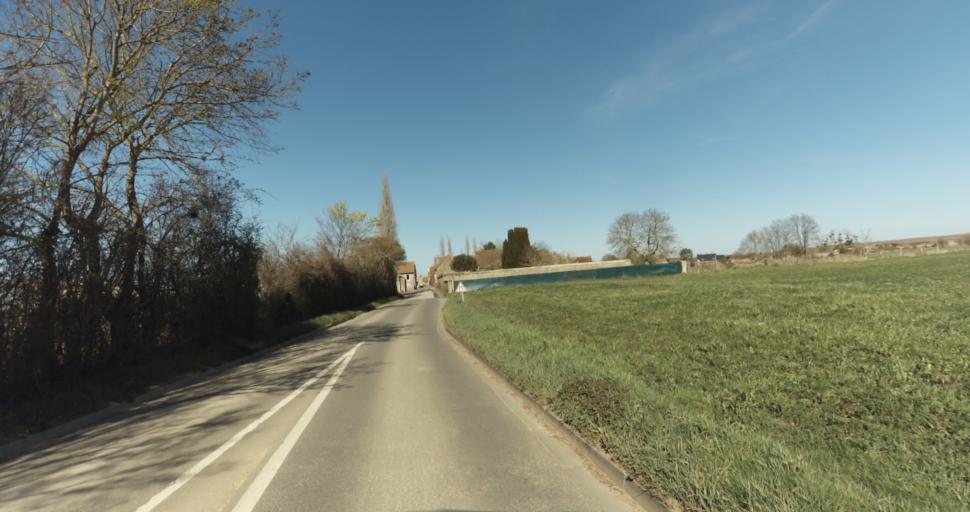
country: FR
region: Lower Normandy
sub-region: Departement du Calvados
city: Canon
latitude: 49.0502
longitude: -0.0648
